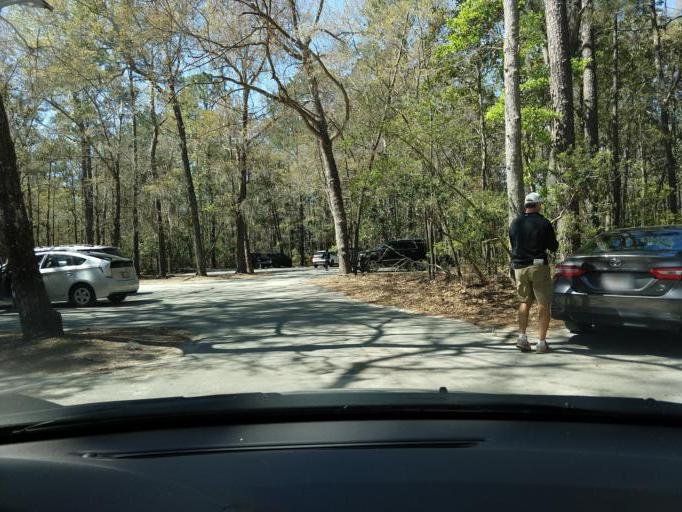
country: US
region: Georgia
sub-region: Chatham County
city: Isle of Hope
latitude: 31.9633
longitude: -81.0698
